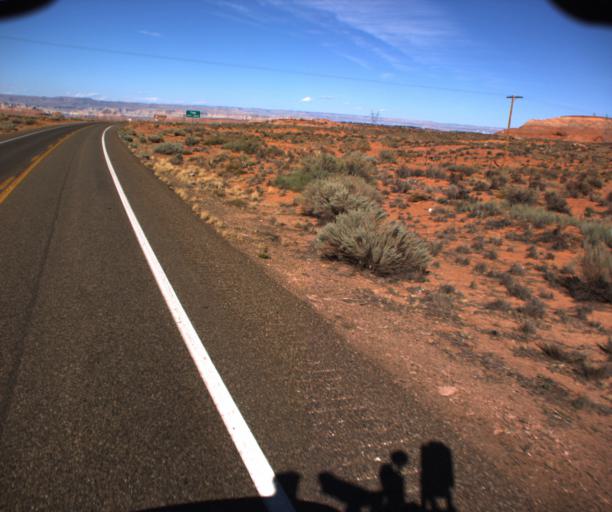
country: US
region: Arizona
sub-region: Coconino County
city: Page
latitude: 36.8740
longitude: -111.5018
